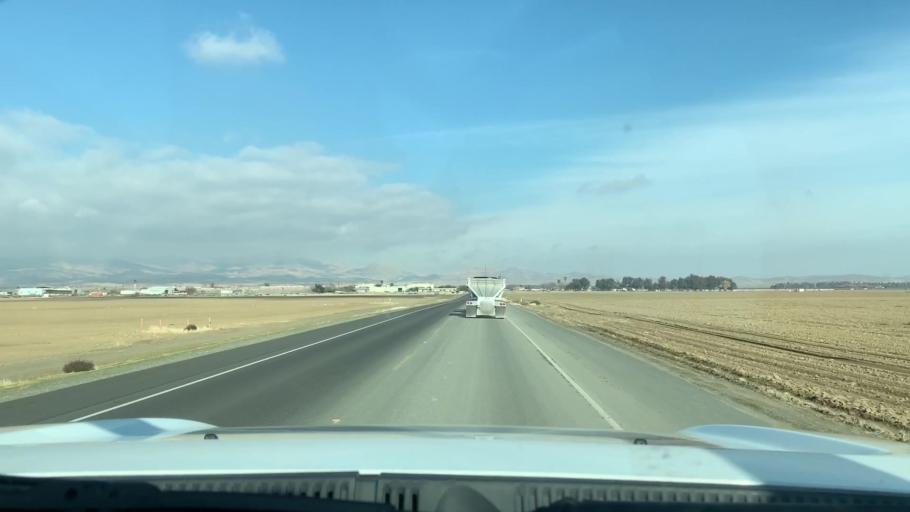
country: US
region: California
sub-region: Fresno County
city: Coalinga
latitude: 36.1711
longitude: -120.3546
